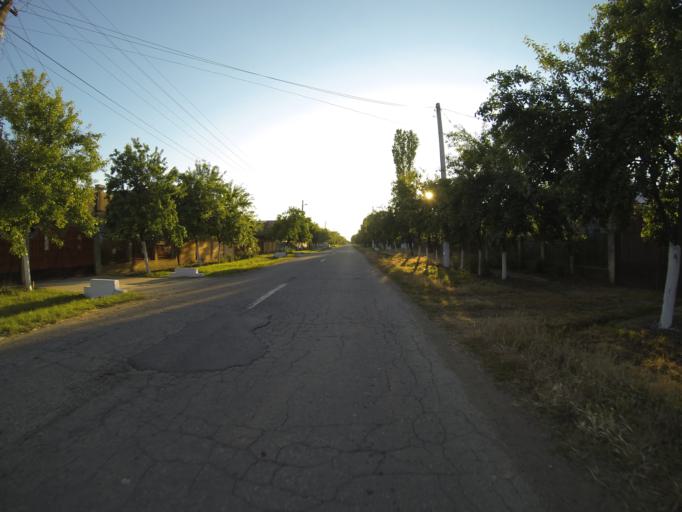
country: RO
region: Dolj
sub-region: Comuna Caloparu
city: Calopar
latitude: 44.1649
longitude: 23.7507
